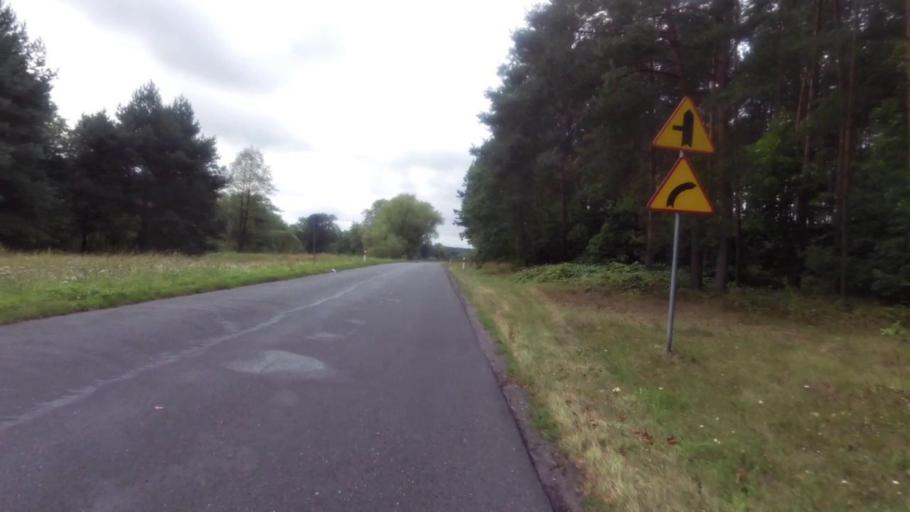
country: PL
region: West Pomeranian Voivodeship
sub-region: Powiat mysliborski
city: Boleszkowice
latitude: 52.6857
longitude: 14.6252
